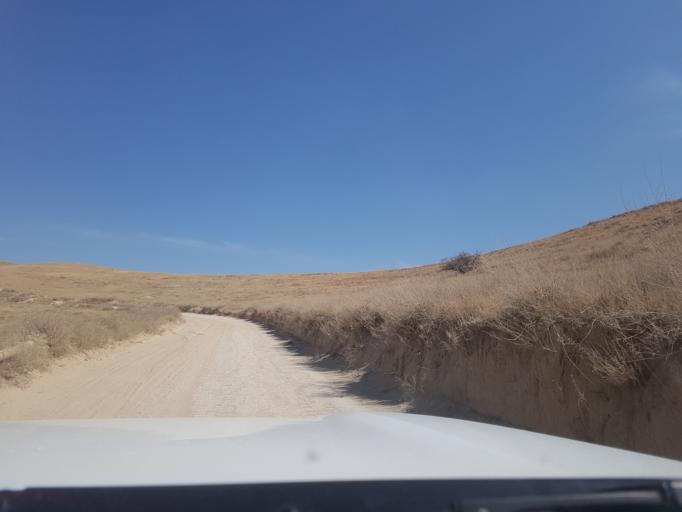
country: TM
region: Ahal
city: Baharly
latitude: 38.2702
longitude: 56.8946
